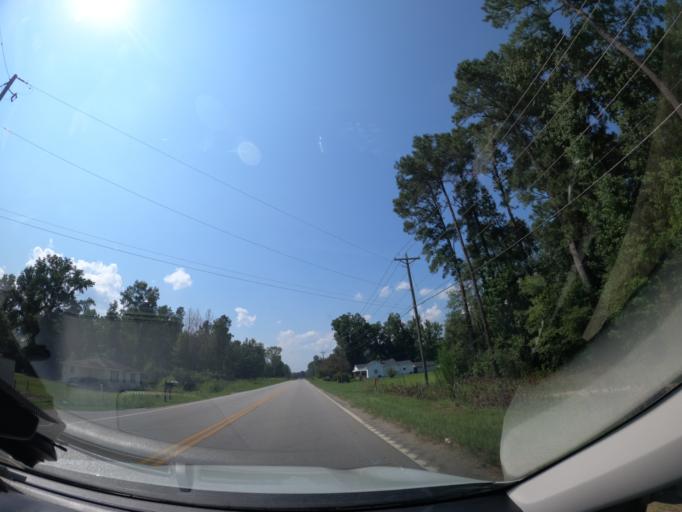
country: US
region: South Carolina
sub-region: Richland County
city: Hopkins
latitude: 33.9293
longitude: -80.9661
